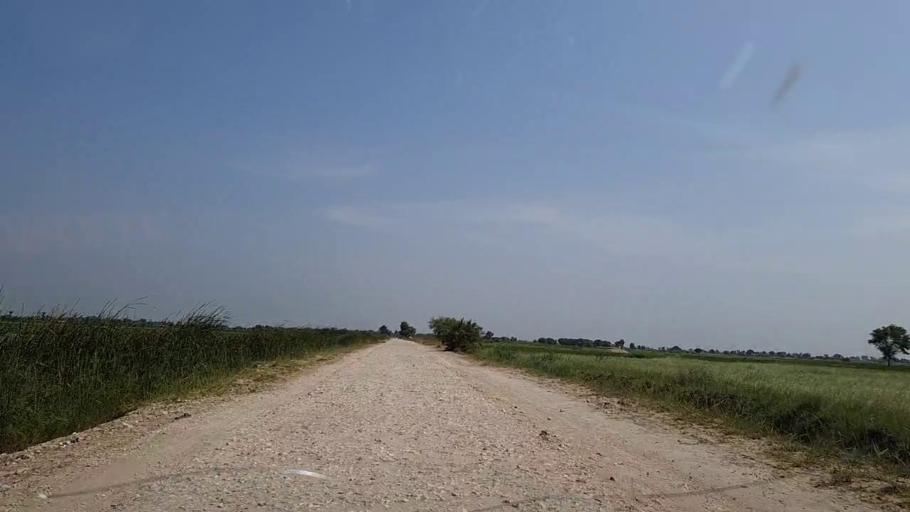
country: PK
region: Sindh
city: Khanpur
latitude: 27.7961
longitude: 69.3150
